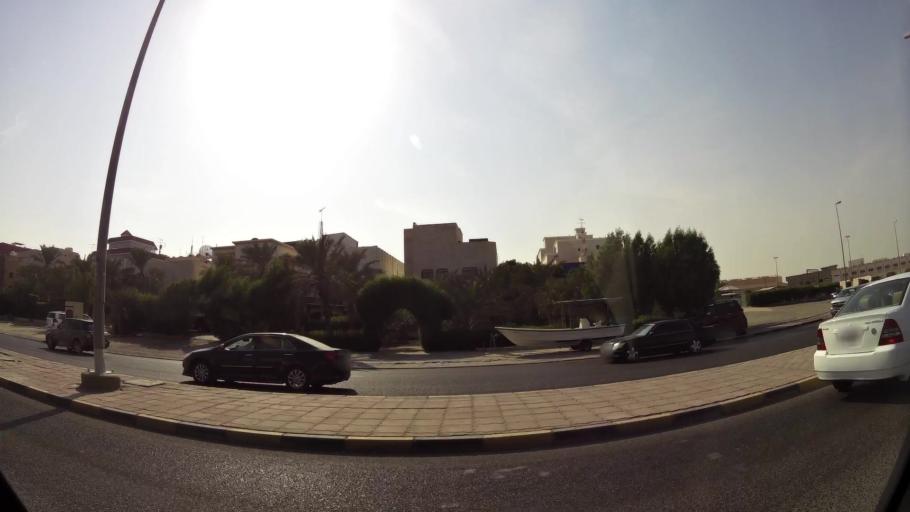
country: KW
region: Mubarak al Kabir
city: Mubarak al Kabir
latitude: 29.1837
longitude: 48.0812
